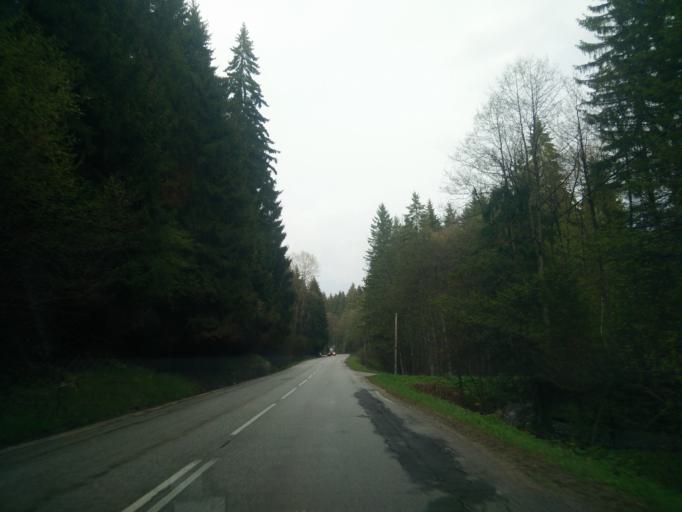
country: SK
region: Banskobystricky
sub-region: Okres Ziar nad Hronom
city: Kremnica
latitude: 48.8372
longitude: 18.9154
